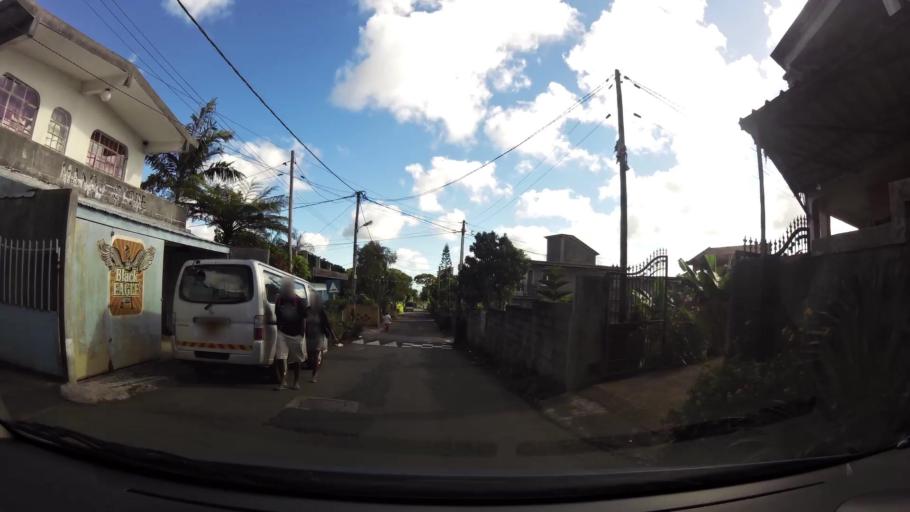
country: MU
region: Plaines Wilhems
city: Curepipe
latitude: -20.3058
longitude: 57.5172
